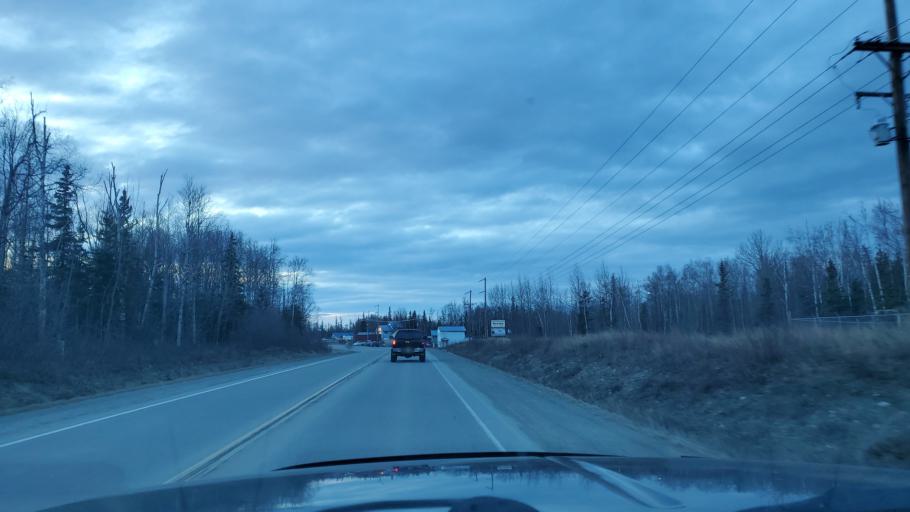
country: US
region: Alaska
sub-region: Matanuska-Susitna Borough
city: Tanaina
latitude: 61.5936
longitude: -149.3872
